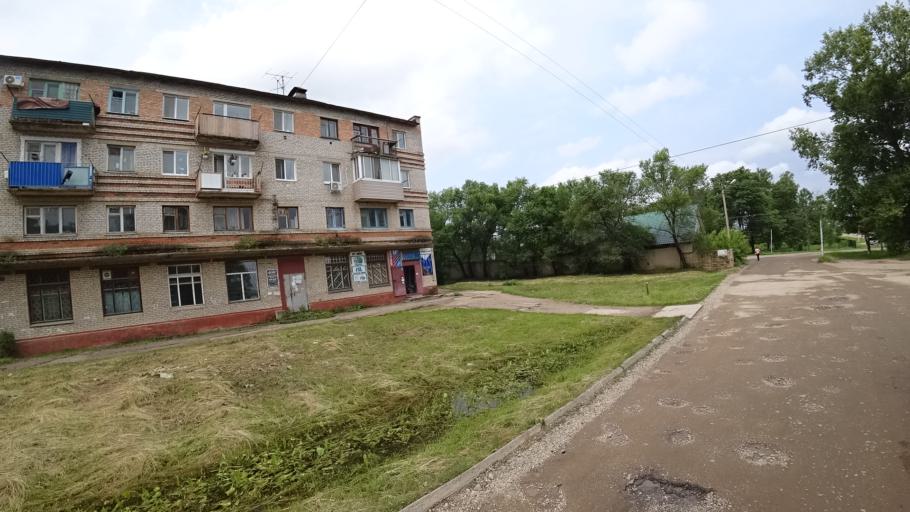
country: RU
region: Primorskiy
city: Novosysoyevka
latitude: 44.2286
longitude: 133.3610
